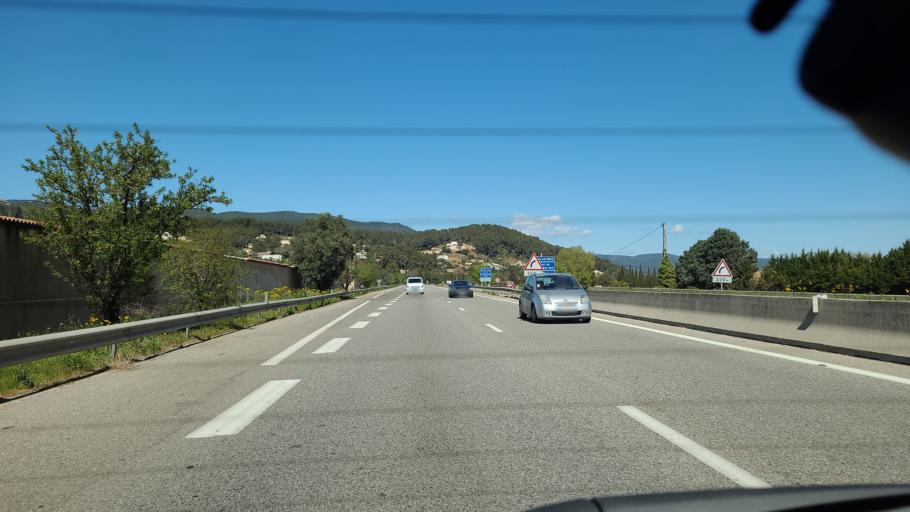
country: FR
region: Provence-Alpes-Cote d'Azur
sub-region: Departement du Var
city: Cuers
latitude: 43.2385
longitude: 6.0843
